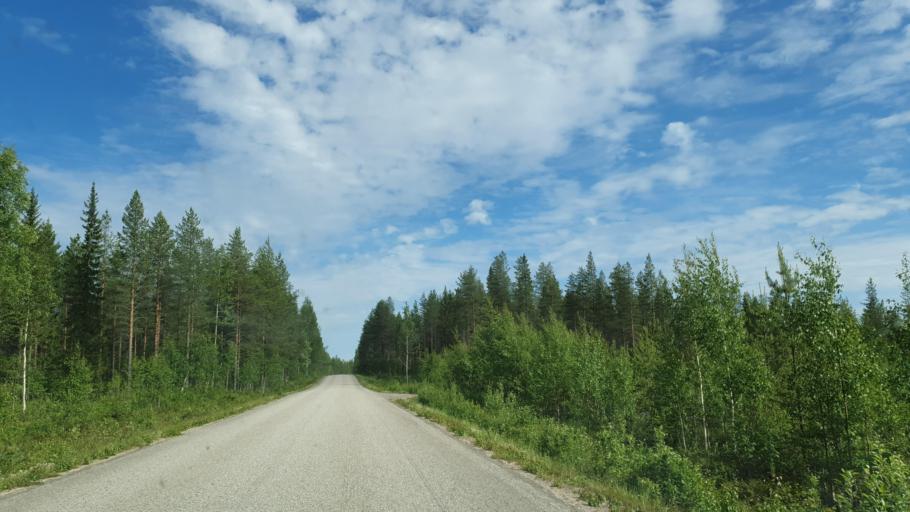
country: FI
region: Kainuu
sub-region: Kehys-Kainuu
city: Kuhmo
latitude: 64.5297
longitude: 29.3538
